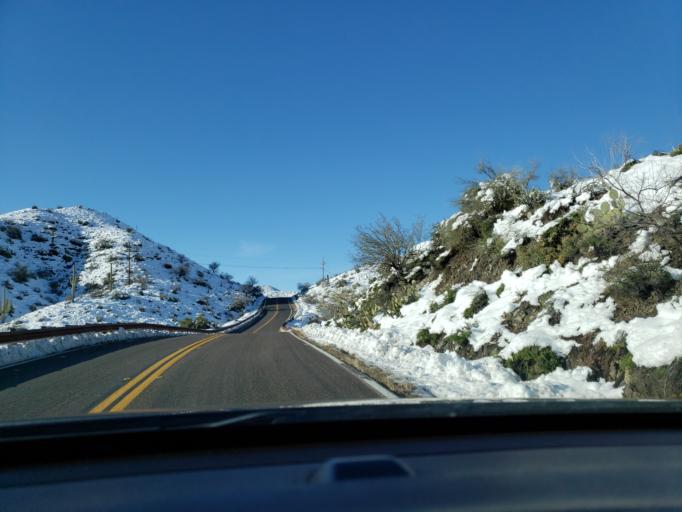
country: US
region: Arizona
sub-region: Maricopa County
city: Carefree
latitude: 33.8859
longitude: -111.8182
